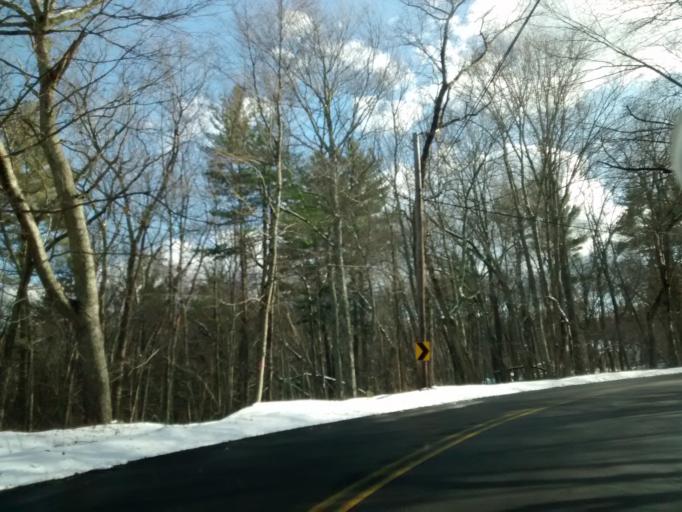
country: US
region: Massachusetts
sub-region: Worcester County
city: Uxbridge
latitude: 42.0464
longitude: -71.6686
